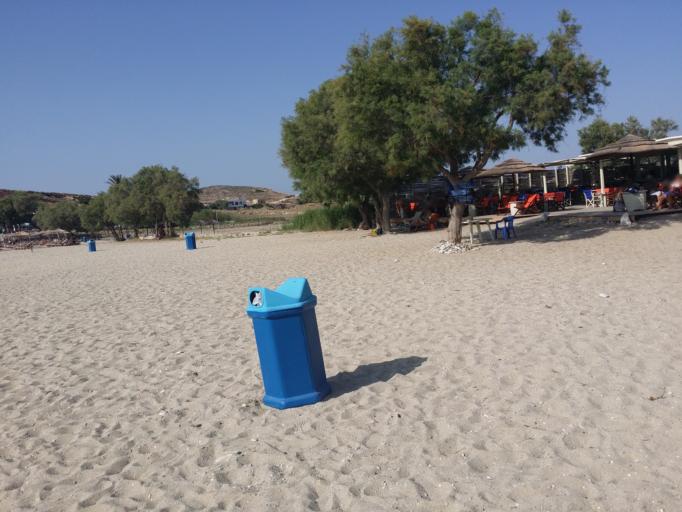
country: GR
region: South Aegean
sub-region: Nomos Kykladon
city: Paros
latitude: 37.0714
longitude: 25.1273
